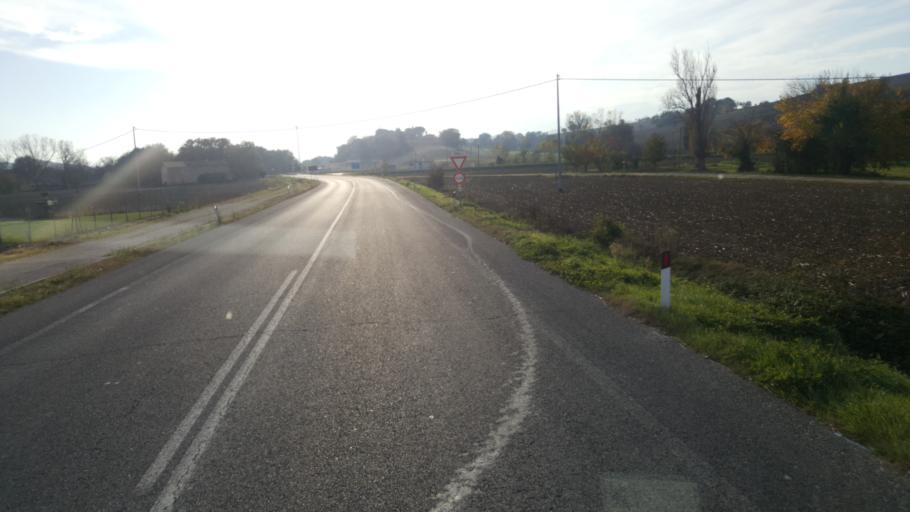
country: IT
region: The Marches
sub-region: Provincia di Ancona
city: Casine
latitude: 43.6438
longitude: 13.1419
